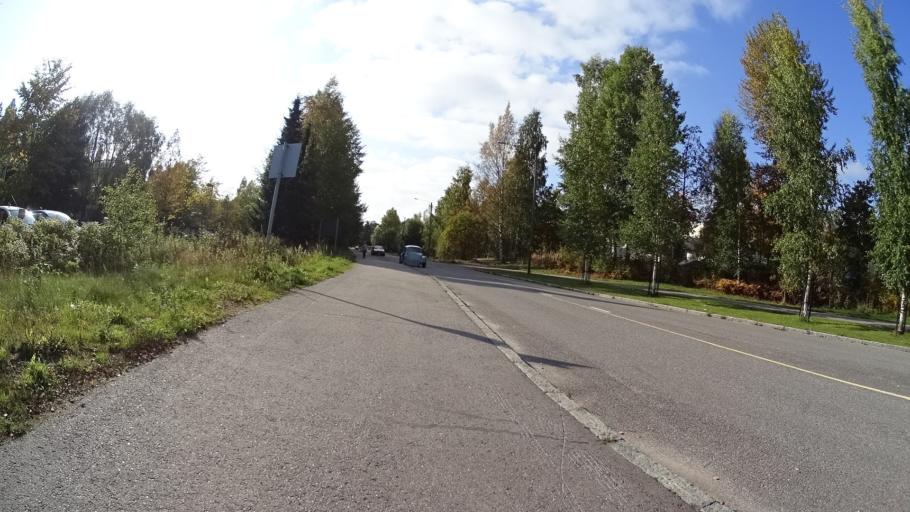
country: FI
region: Uusimaa
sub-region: Helsinki
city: Kilo
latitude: 60.2376
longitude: 24.8214
